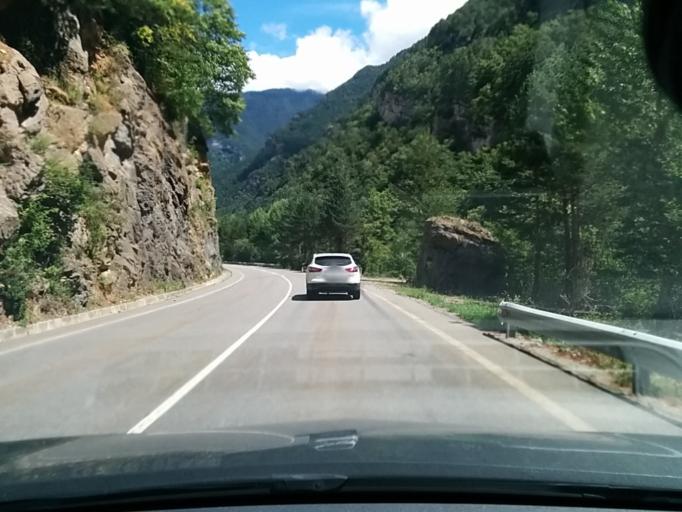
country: ES
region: Aragon
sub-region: Provincia de Huesca
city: Bielsa
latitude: 42.5894
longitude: 0.2315
